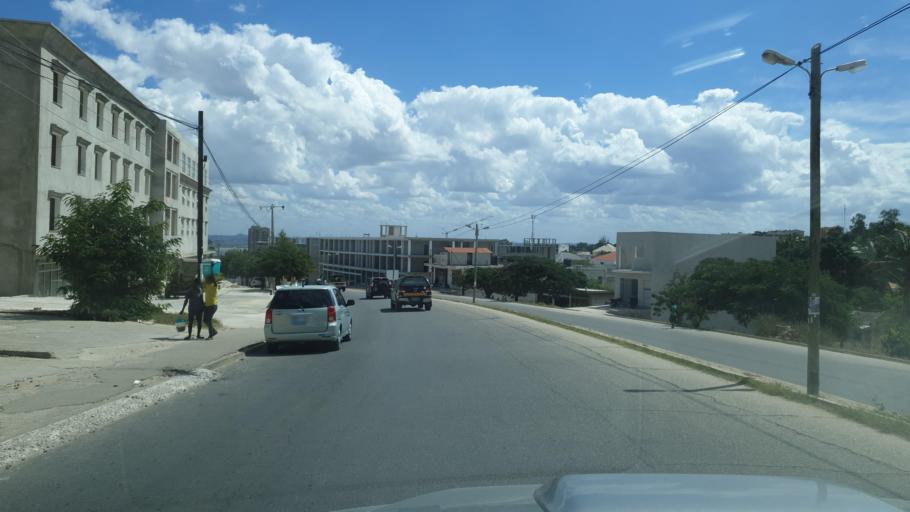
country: MZ
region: Nampula
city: Nacala
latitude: -14.5440
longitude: 40.6819
